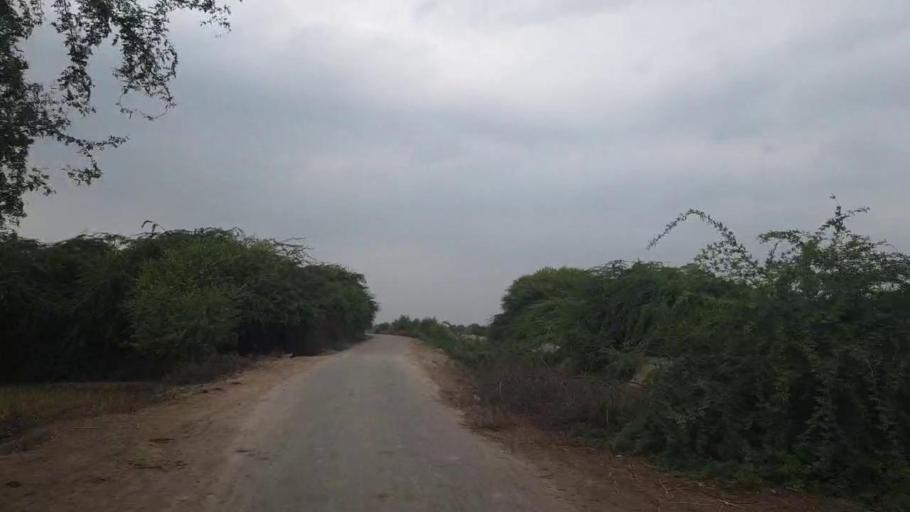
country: PK
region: Sindh
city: Badin
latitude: 24.6246
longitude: 68.6822
